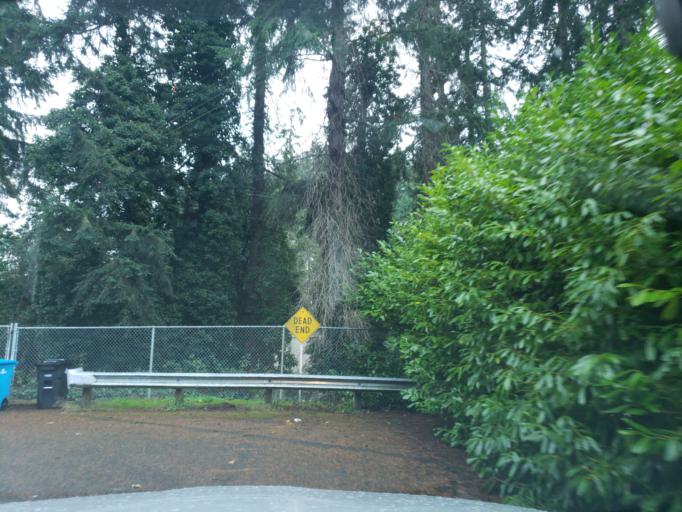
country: US
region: Washington
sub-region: Snohomish County
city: Esperance
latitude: 47.7688
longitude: -122.3571
